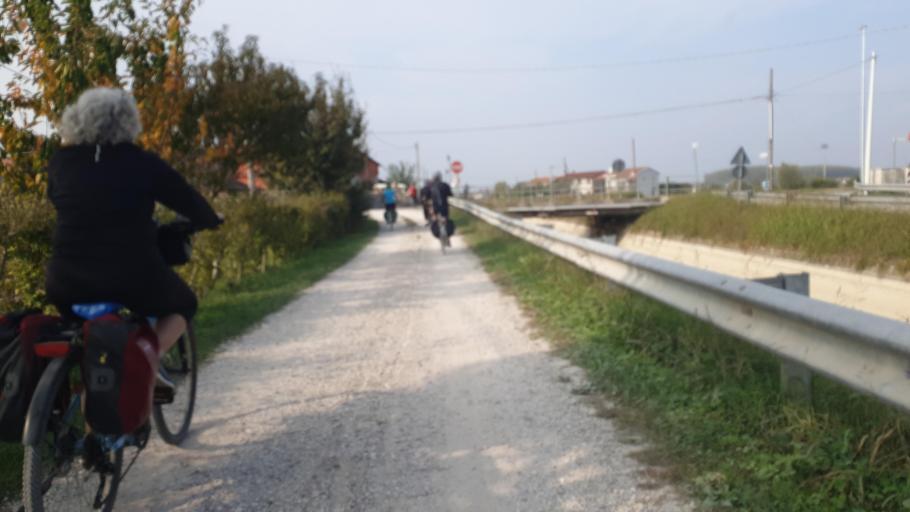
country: IT
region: Veneto
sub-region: Provincia di Padova
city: Corte
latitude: 45.2973
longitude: 12.0816
